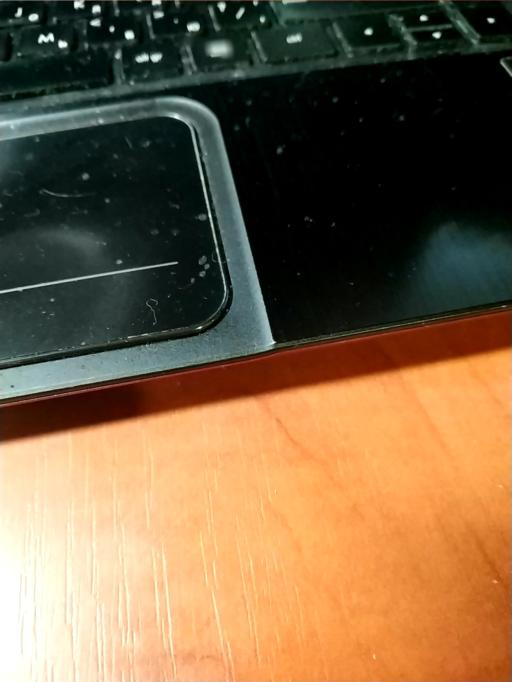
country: RU
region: Kostroma
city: Kosmynino
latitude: 57.6426
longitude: 40.8046
